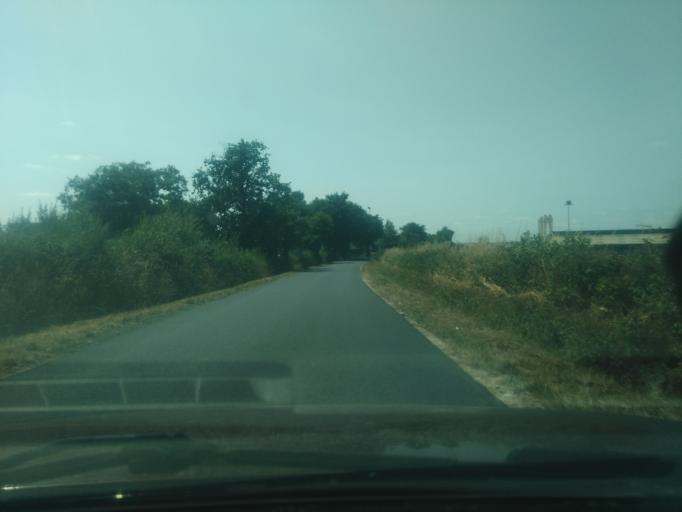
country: FR
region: Pays de la Loire
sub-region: Departement de la Vendee
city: Vendrennes
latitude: 46.7992
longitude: -1.1421
